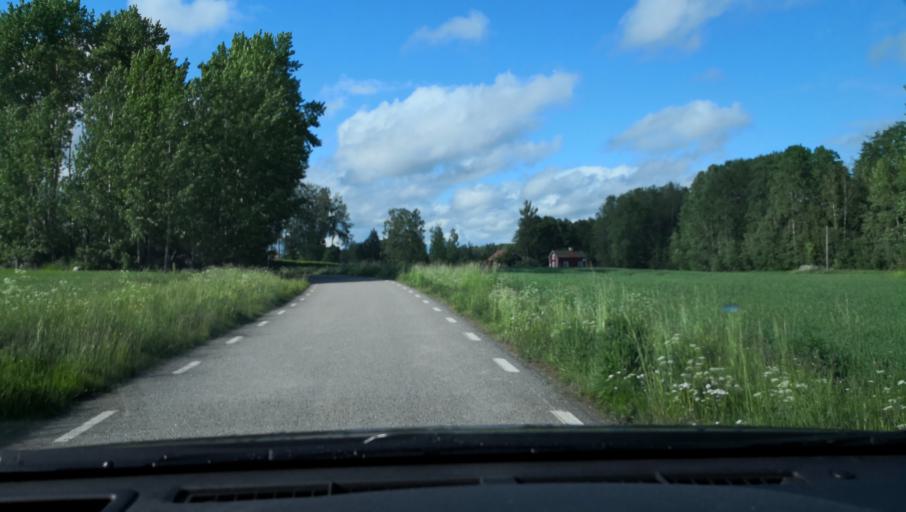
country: SE
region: OErebro
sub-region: Lindesbergs Kommun
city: Fellingsbro
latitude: 59.3340
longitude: 15.6854
